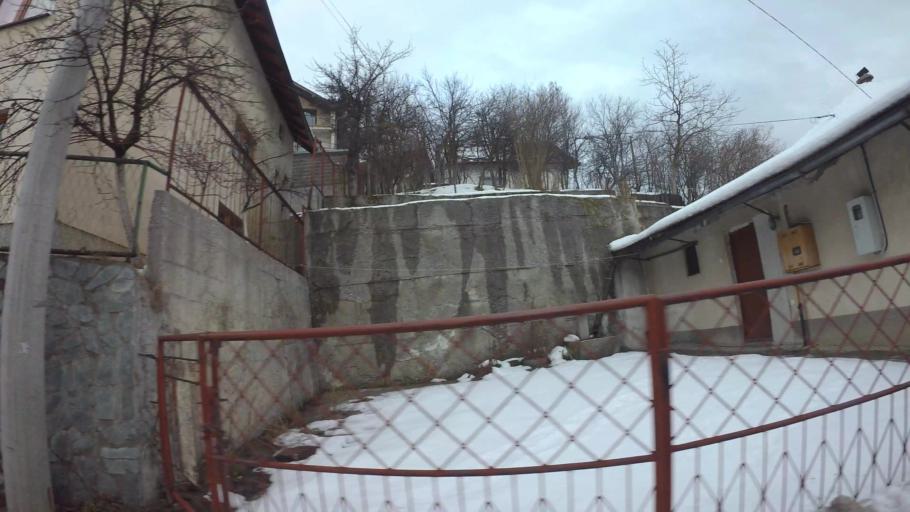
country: BA
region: Federation of Bosnia and Herzegovina
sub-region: Kanton Sarajevo
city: Sarajevo
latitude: 43.8561
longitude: 18.3579
